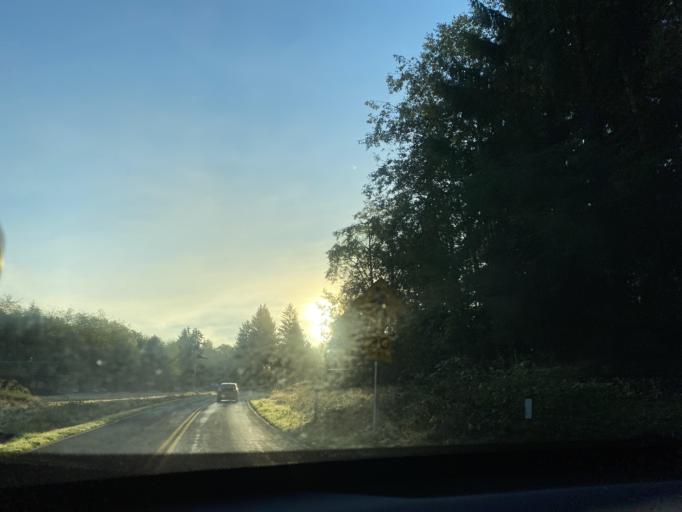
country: US
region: Washington
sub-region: Clallam County
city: Forks
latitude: 47.8167
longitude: -124.1588
